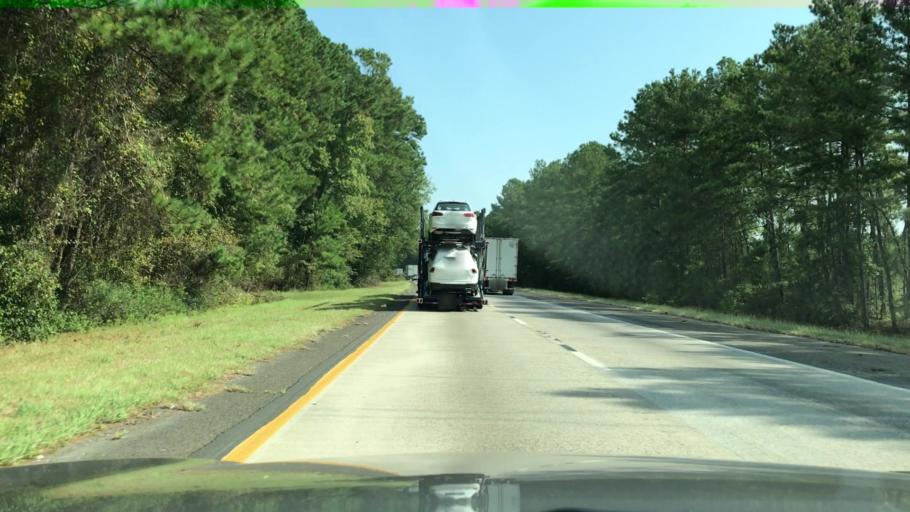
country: US
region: South Carolina
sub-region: Colleton County
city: Walterboro
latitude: 32.8238
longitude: -80.7510
